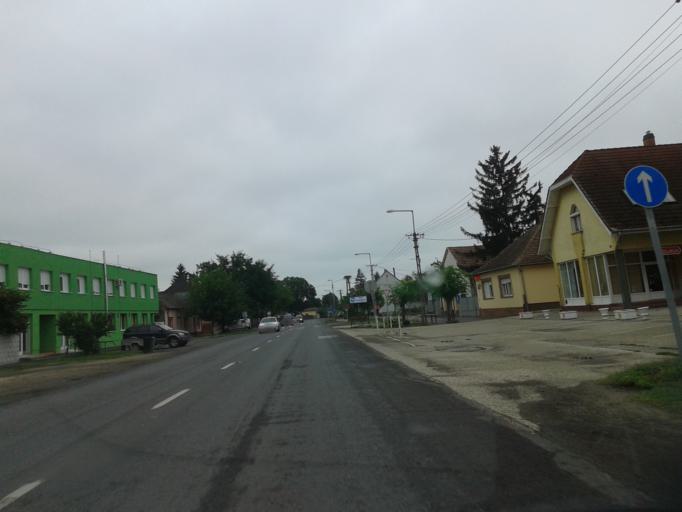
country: HU
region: Bacs-Kiskun
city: Akaszto
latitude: 46.6927
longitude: 19.2038
